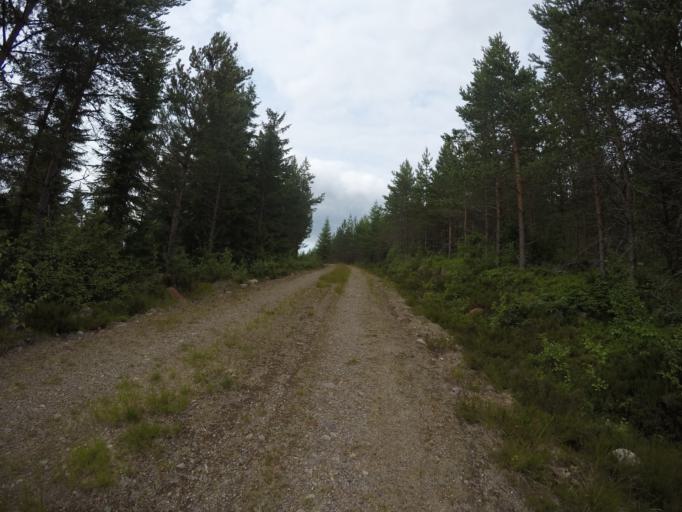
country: SE
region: Vaermland
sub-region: Filipstads Kommun
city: Lesjofors
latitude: 60.2123
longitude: 14.2619
